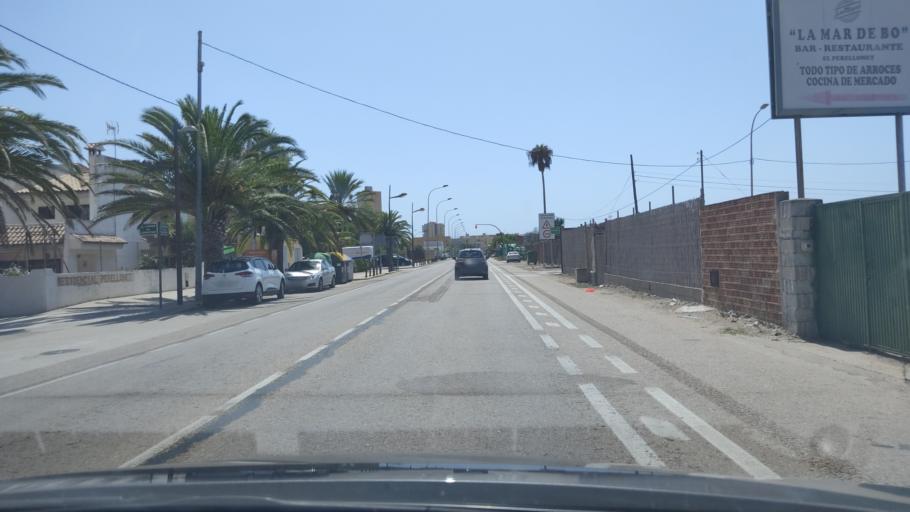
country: ES
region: Valencia
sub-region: Provincia de Valencia
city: Sollana
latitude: 39.3067
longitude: -0.2965
